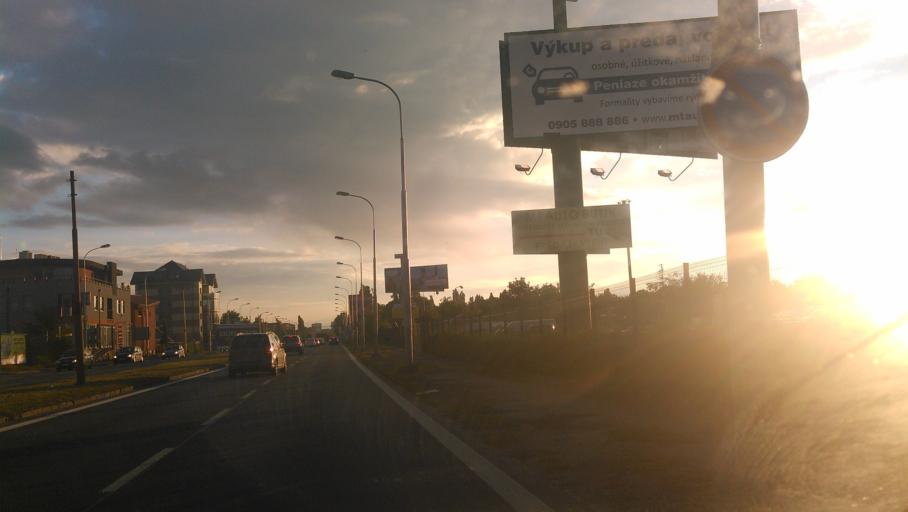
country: SK
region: Bratislavsky
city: Bratislava
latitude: 48.1771
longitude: 17.1666
